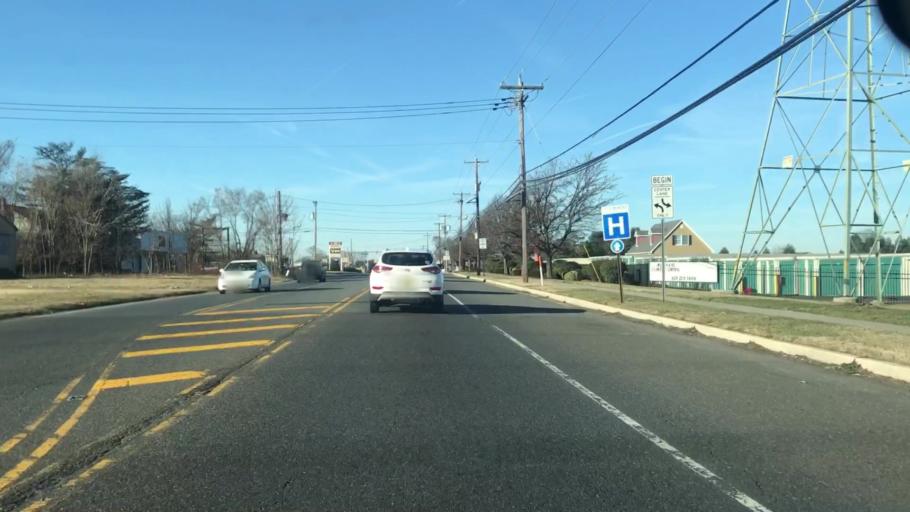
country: US
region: New Jersey
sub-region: Burlington County
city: Willingboro
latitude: 40.0496
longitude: -74.8729
